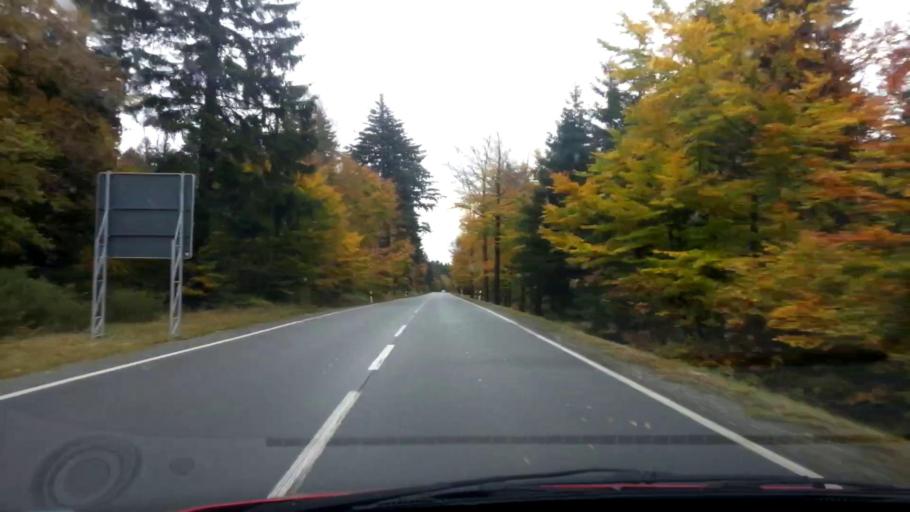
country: DE
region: Bavaria
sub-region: Upper Franconia
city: Fichtelberg
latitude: 50.0069
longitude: 11.8281
